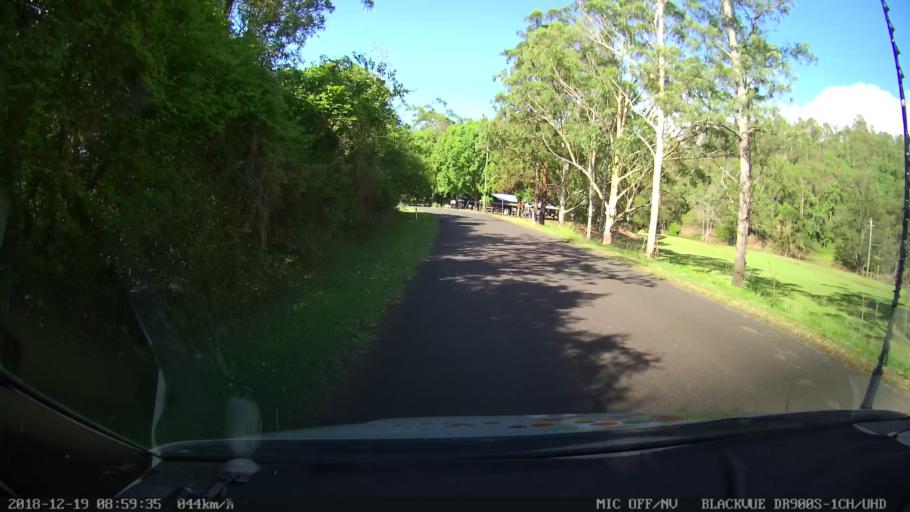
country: AU
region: New South Wales
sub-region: Kyogle
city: Kyogle
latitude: -28.4276
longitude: 152.9588
